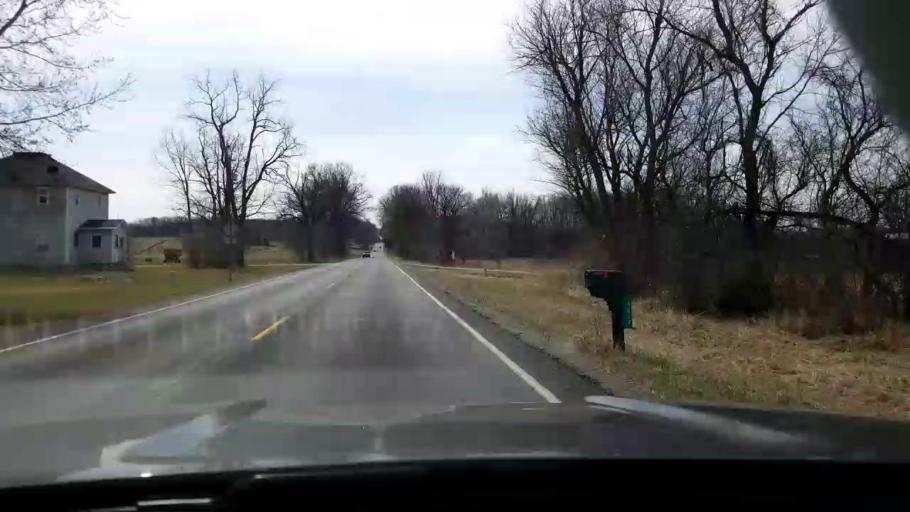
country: US
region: Michigan
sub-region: Jackson County
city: Spring Arbor
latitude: 42.1952
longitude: -84.5208
